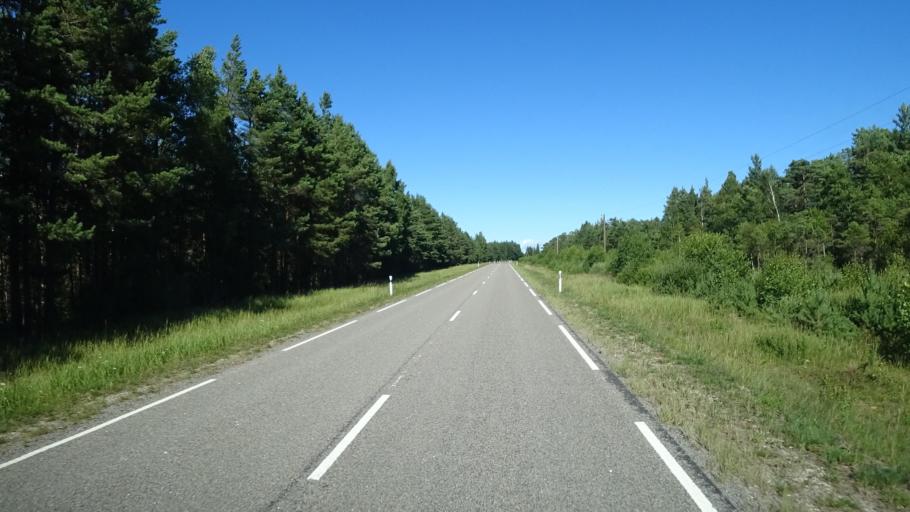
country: LV
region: Dundaga
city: Dundaga
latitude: 57.6964
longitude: 22.4030
